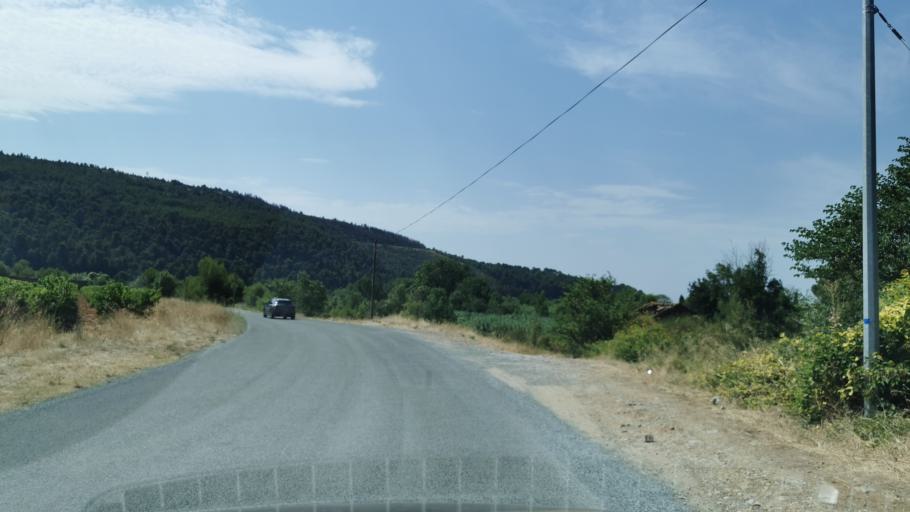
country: FR
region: Languedoc-Roussillon
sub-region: Departement de l'Aude
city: Bize-Minervois
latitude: 43.3269
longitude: 2.8787
